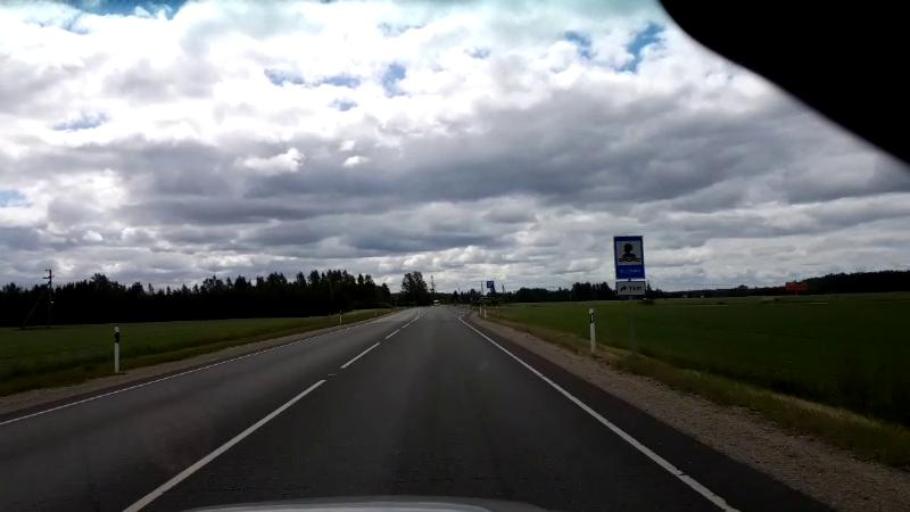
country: EE
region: Paernumaa
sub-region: Paikuse vald
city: Paikuse
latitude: 58.3066
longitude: 24.6088
